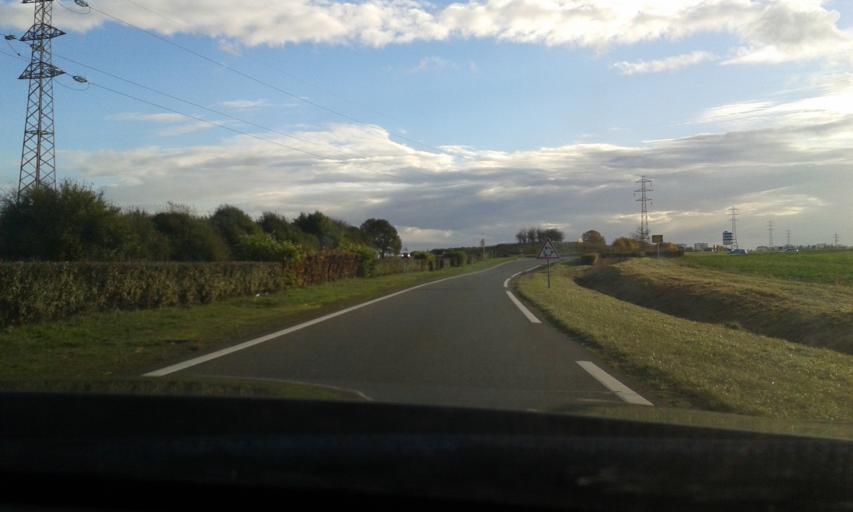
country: FR
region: Centre
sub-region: Departement d'Eure-et-Loir
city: Leves
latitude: 48.4686
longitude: 1.4650
